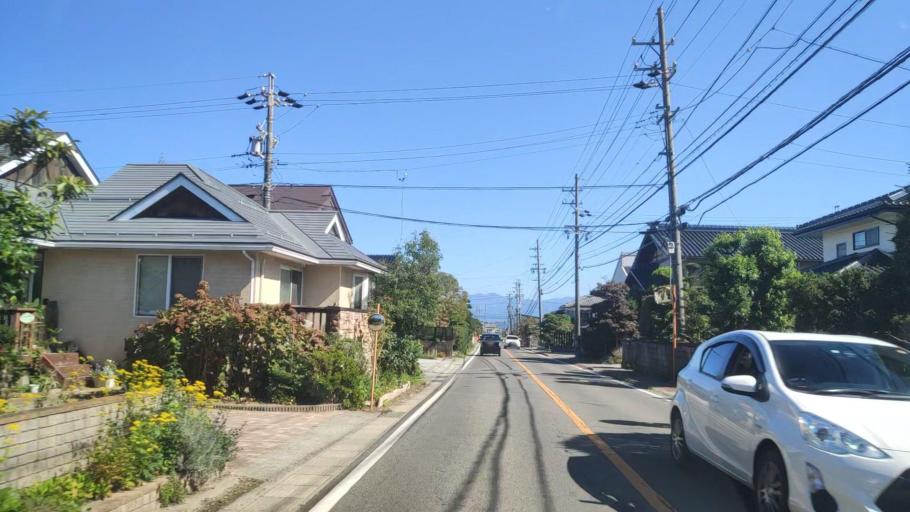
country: JP
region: Nagano
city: Shiojiri
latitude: 36.1428
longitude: 137.9417
